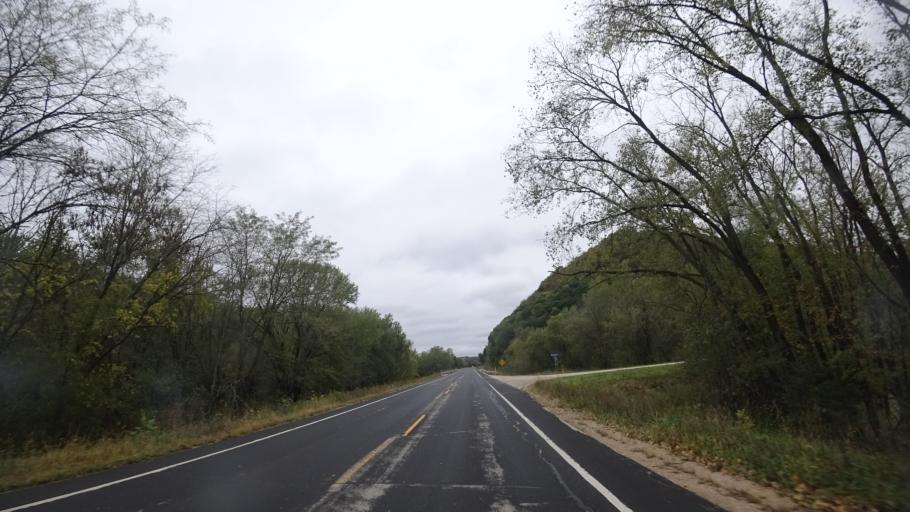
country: US
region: Wisconsin
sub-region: Grant County
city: Boscobel
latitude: 43.1855
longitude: -90.6724
